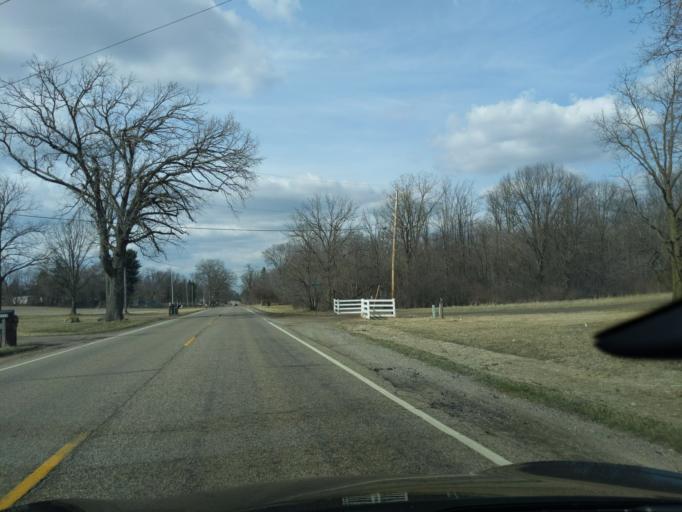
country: US
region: Michigan
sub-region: Jackson County
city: Jackson
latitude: 42.3325
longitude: -84.4136
